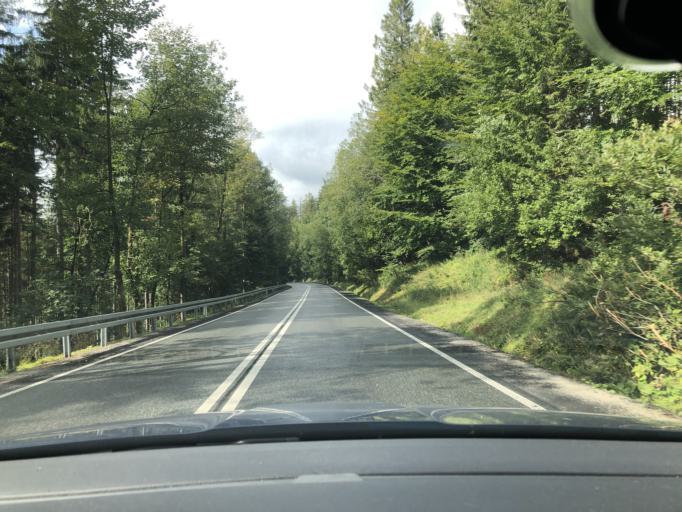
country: PL
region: Lesser Poland Voivodeship
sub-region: Powiat suski
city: Zawoja
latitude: 49.5965
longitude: 19.5819
